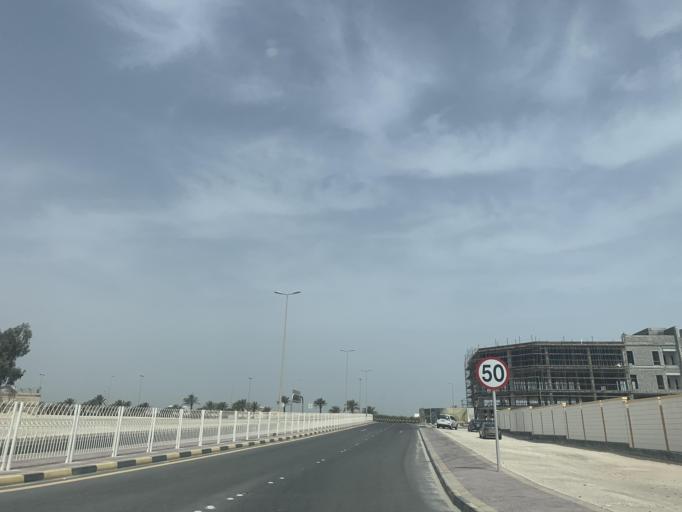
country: BH
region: Northern
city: Madinat `Isa
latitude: 26.1596
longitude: 50.5405
